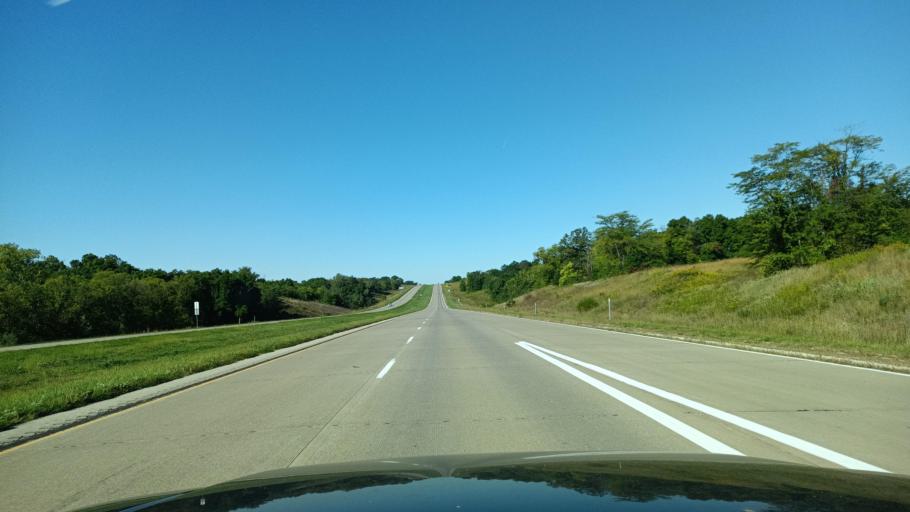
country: US
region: Iowa
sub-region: Lee County
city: Fort Madison
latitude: 40.6707
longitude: -91.2789
